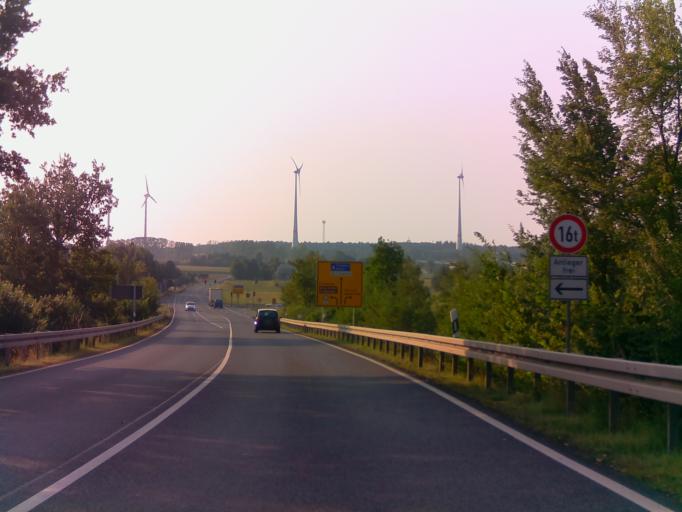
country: DE
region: Hesse
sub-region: Regierungsbezirk Kassel
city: Friedewald
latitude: 50.8831
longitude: 9.8688
